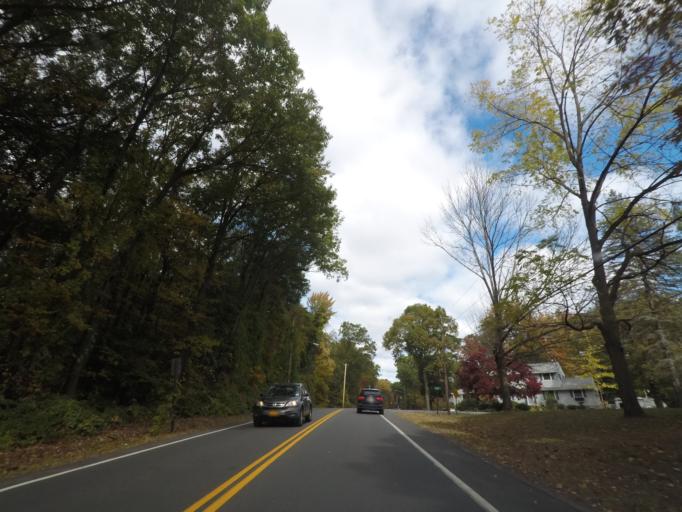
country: US
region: New York
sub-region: Saratoga County
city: Country Knolls
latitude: 42.8485
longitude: -73.7700
